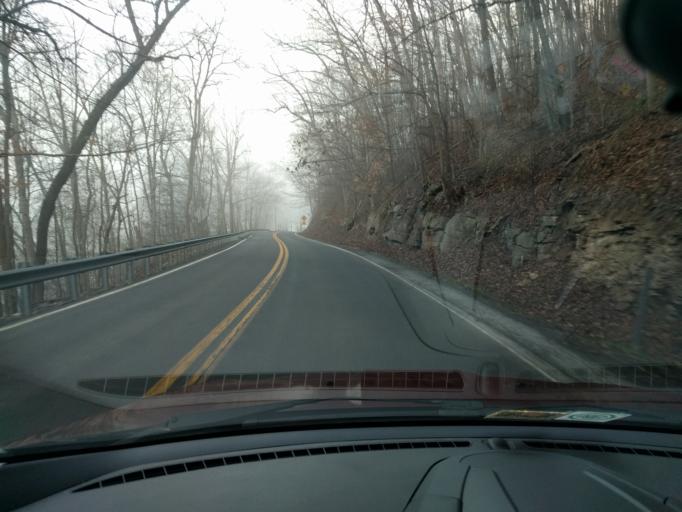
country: US
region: West Virginia
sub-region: Fayette County
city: Ansted
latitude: 38.1284
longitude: -81.1419
